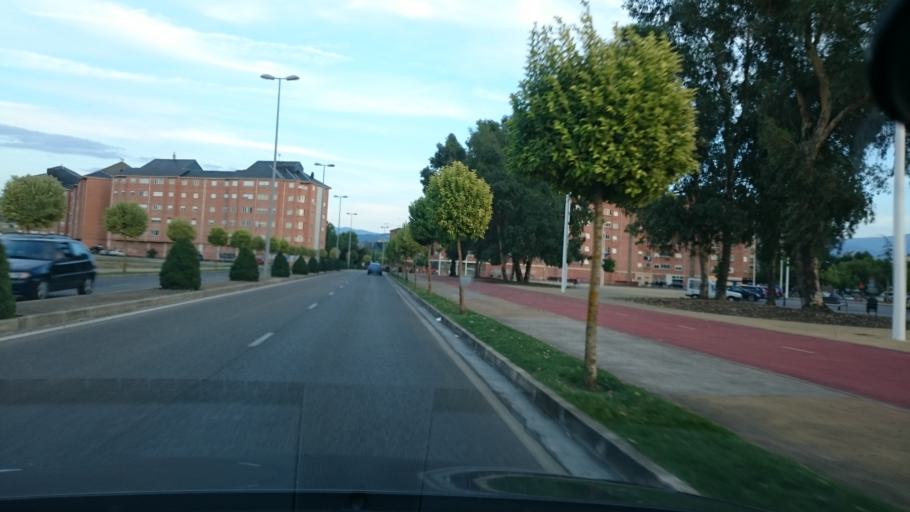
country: ES
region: Castille and Leon
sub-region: Provincia de Leon
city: Ponferrada
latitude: 42.5567
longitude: -6.5970
